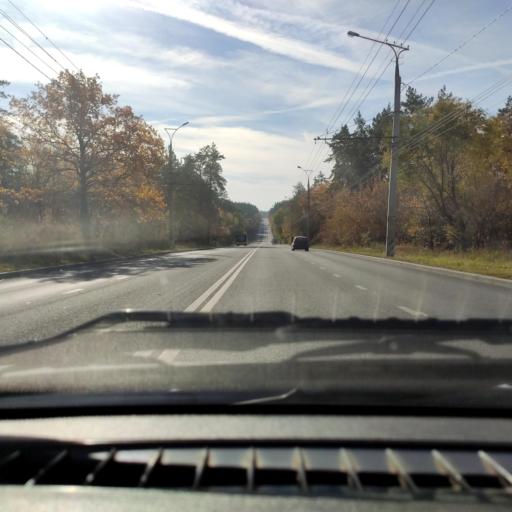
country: RU
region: Samara
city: Zhigulevsk
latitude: 53.5033
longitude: 49.4635
